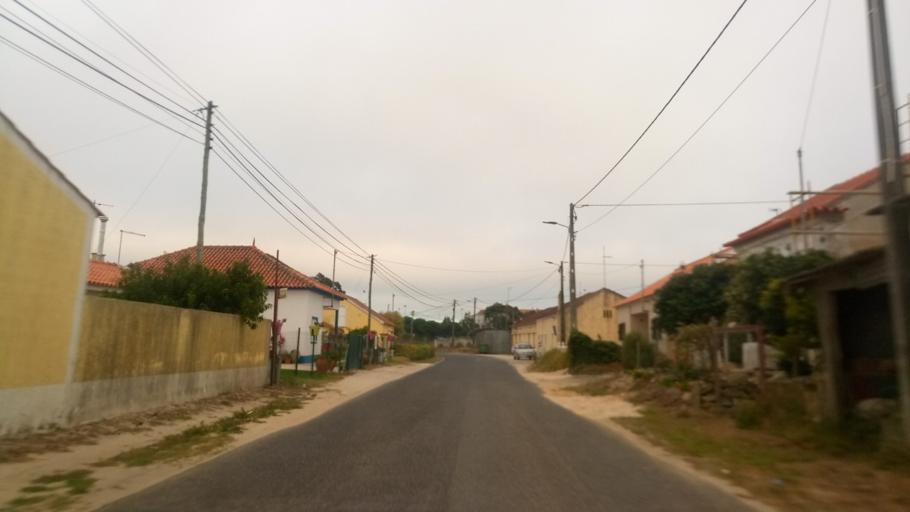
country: PT
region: Leiria
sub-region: Caldas da Rainha
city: Caldas da Rainha
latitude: 39.4181
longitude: -9.1452
